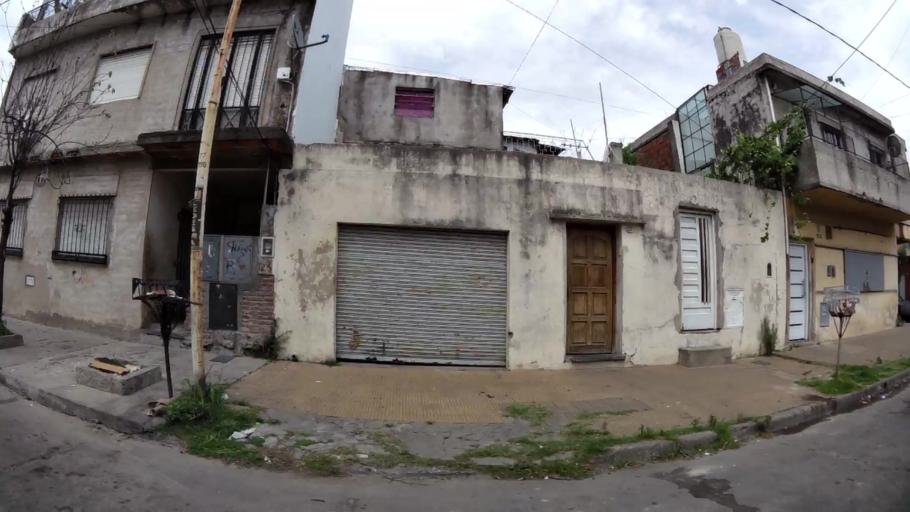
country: AR
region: Buenos Aires F.D.
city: Villa Lugano
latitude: -34.6852
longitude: -58.4993
